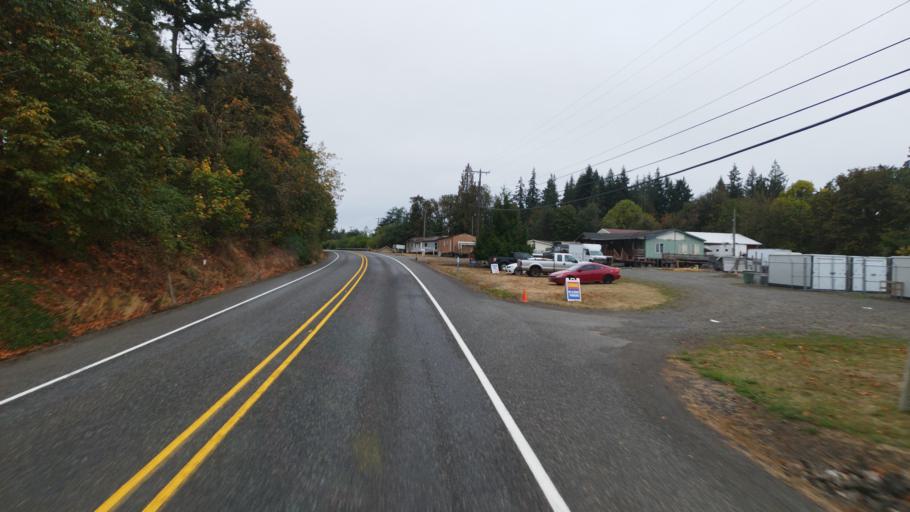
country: US
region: Oregon
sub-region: Columbia County
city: Rainier
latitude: 46.0642
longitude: -122.8963
